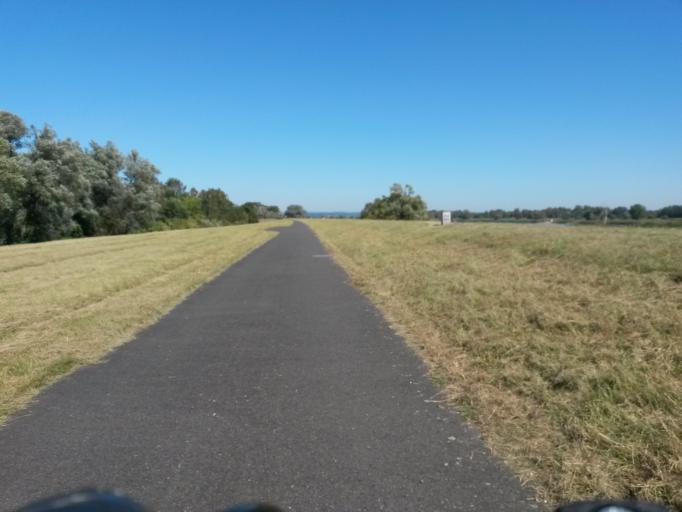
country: PL
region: West Pomeranian Voivodeship
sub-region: Powiat gryfinski
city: Cedynia
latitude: 52.8672
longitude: 14.1442
